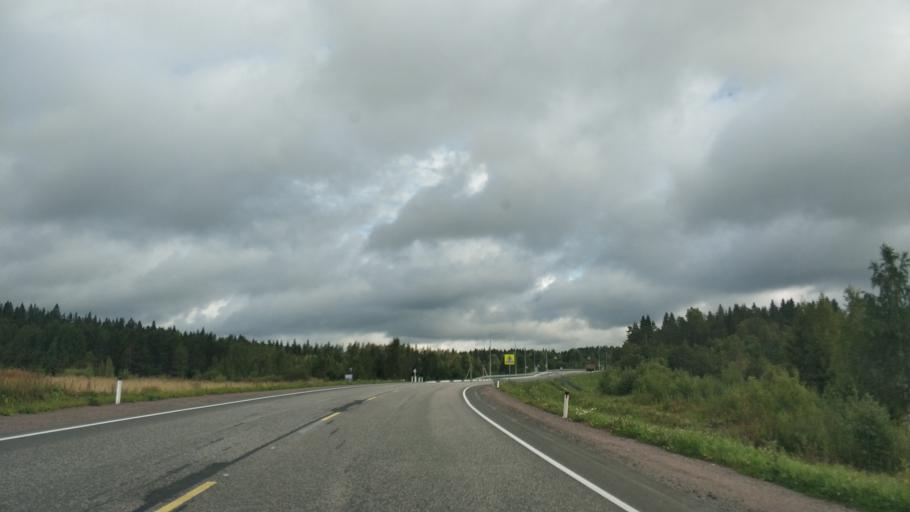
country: RU
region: Republic of Karelia
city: Khelyulya
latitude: 61.7993
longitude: 30.6153
